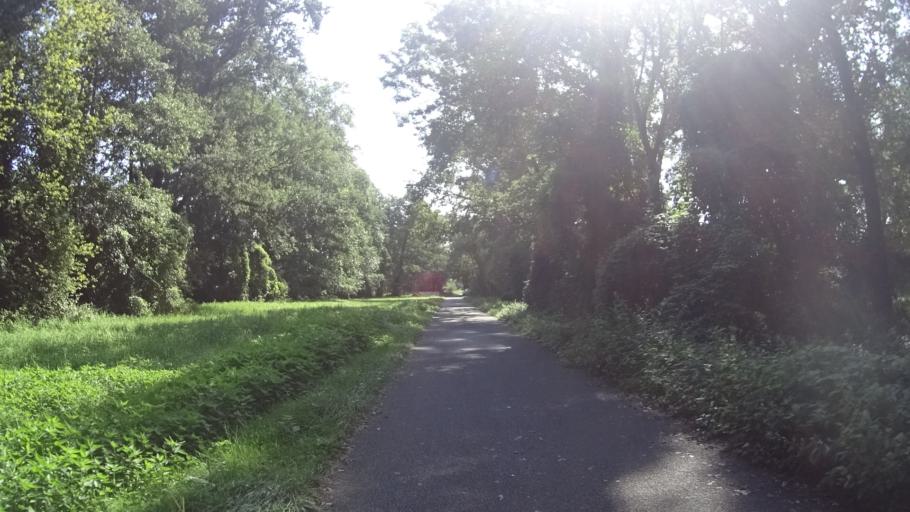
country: DE
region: Brandenburg
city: Burg
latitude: 51.8237
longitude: 14.1573
